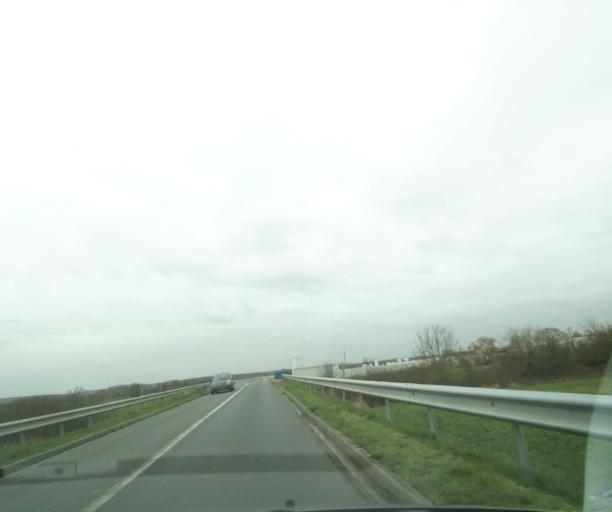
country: FR
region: Picardie
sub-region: Departement de l'Oise
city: Noyon
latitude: 49.5784
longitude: 3.0317
